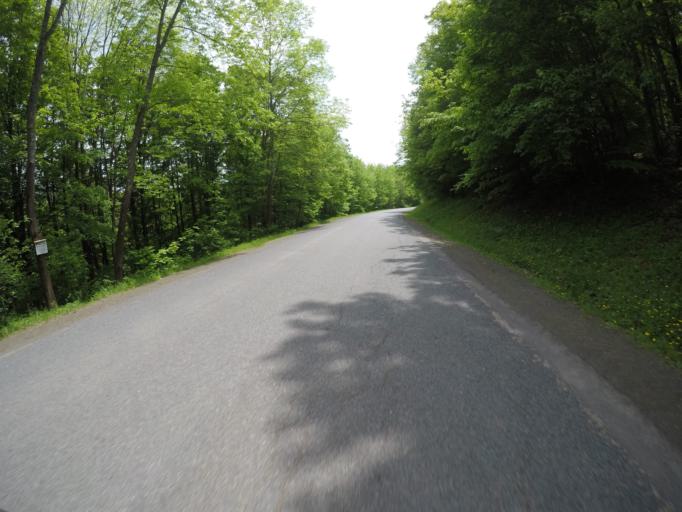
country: US
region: New York
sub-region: Delaware County
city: Stamford
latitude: 42.2314
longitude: -74.6939
